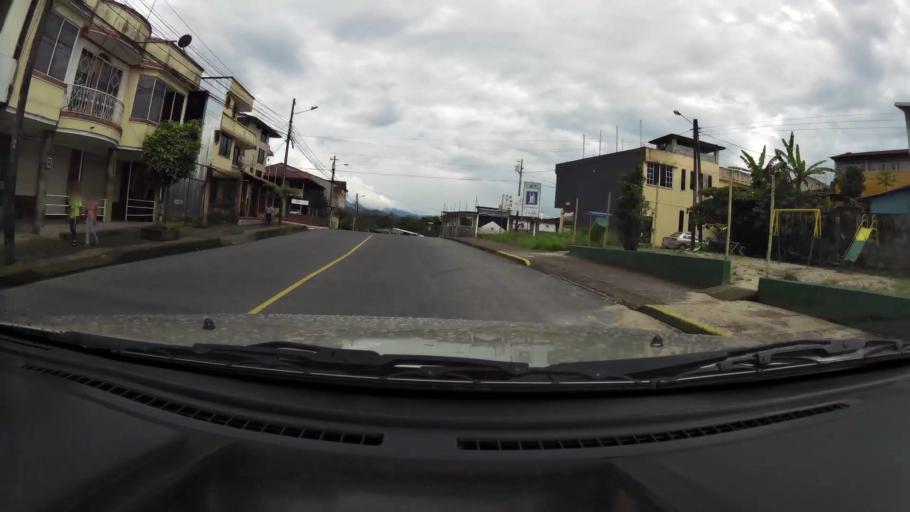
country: EC
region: Pastaza
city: Puyo
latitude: -1.4773
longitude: -78.0002
